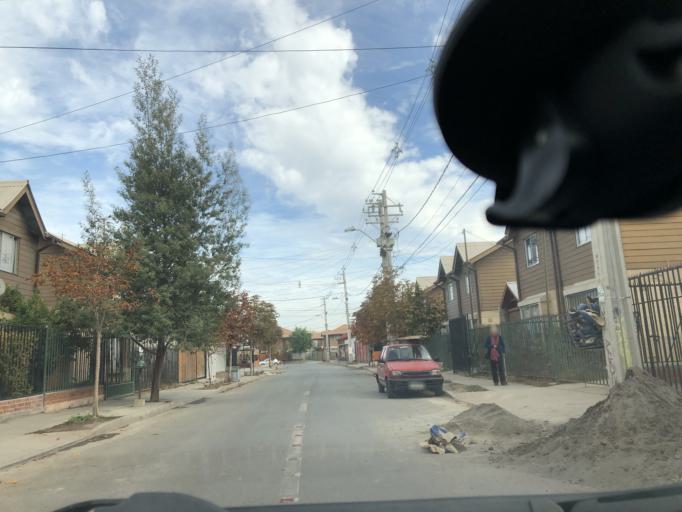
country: CL
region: Santiago Metropolitan
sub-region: Provincia de Cordillera
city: Puente Alto
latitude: -33.6111
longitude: -70.5237
